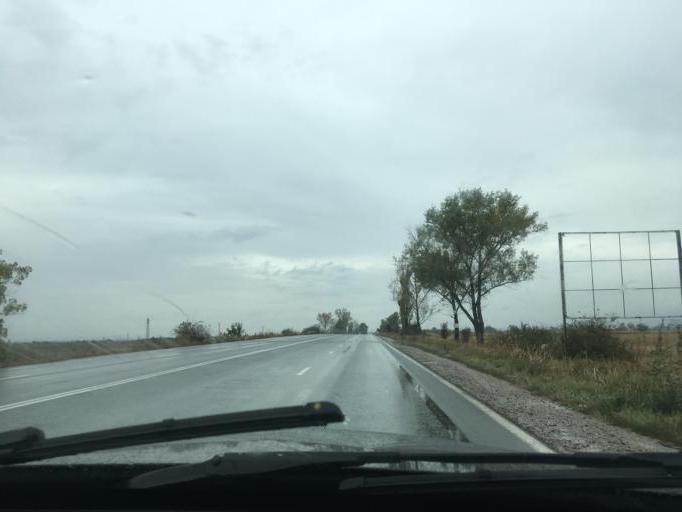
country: BG
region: Sofiya
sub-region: Obshtina Bozhurishte
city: Bozhurishte
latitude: 42.7894
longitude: 23.1555
